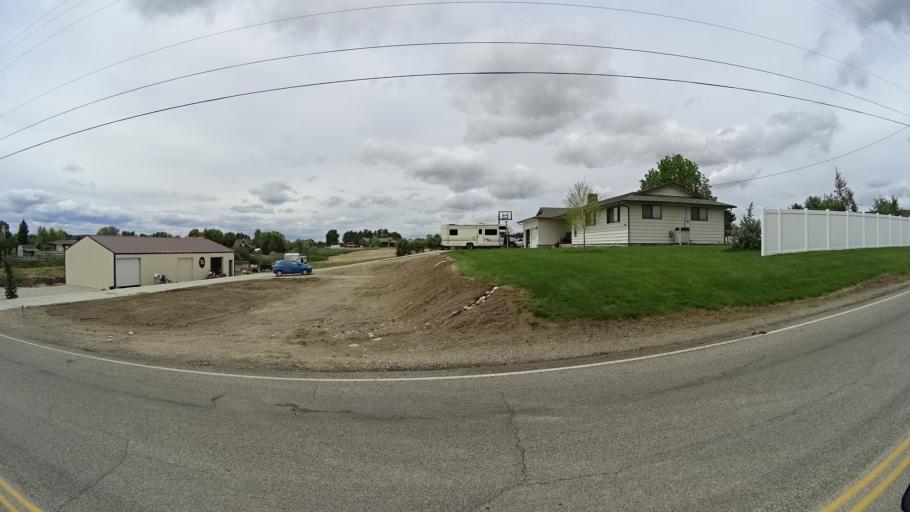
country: US
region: Idaho
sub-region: Ada County
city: Eagle
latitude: 43.7046
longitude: -116.4036
